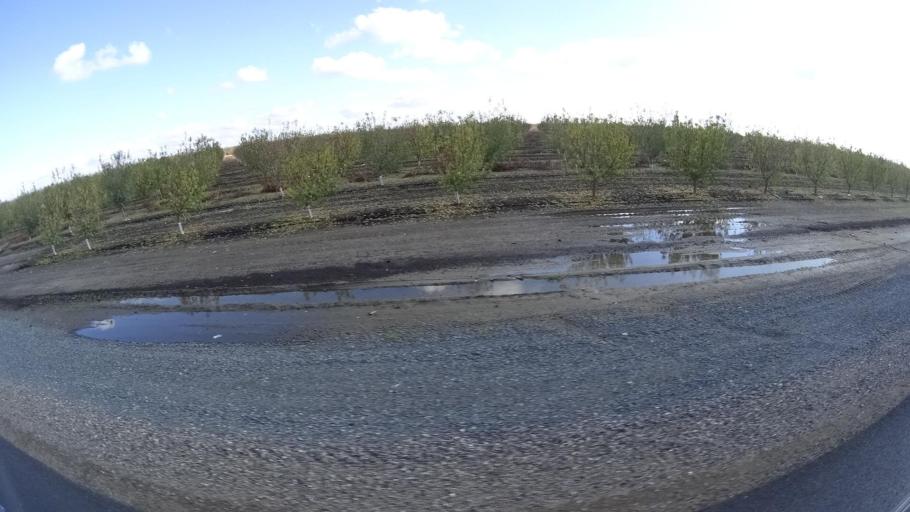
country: US
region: California
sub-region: Kern County
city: Wasco
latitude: 35.6731
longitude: -119.3307
